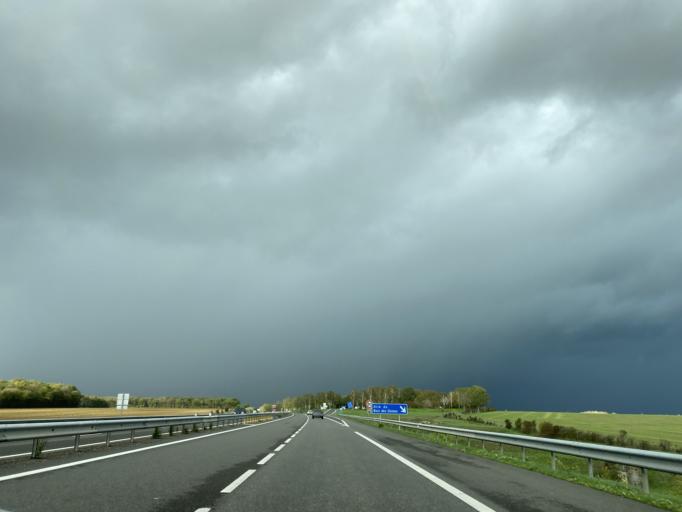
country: FR
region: Centre
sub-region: Departement du Cher
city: Trouy
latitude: 47.0215
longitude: 2.3809
